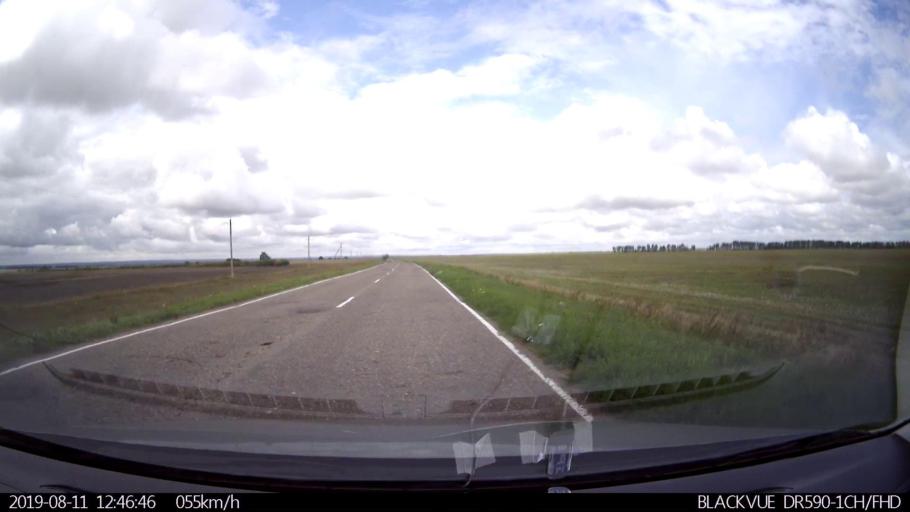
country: RU
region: Ulyanovsk
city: Ignatovka
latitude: 53.8660
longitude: 47.7155
